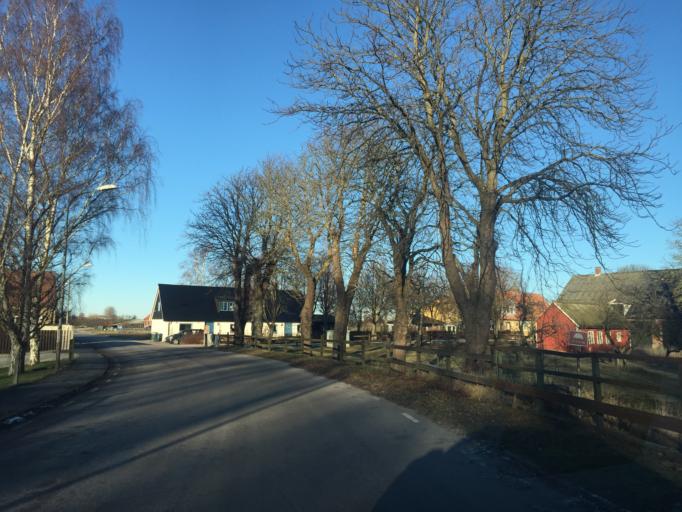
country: SE
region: Skane
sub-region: Kavlinge Kommun
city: Kaevlinge
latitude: 55.7275
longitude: 13.1062
